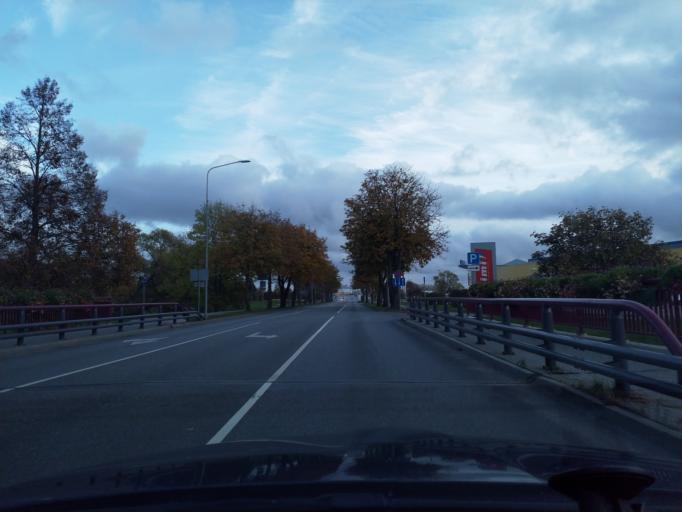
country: LV
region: Ventspils
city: Ventspils
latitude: 57.3888
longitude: 21.5782
